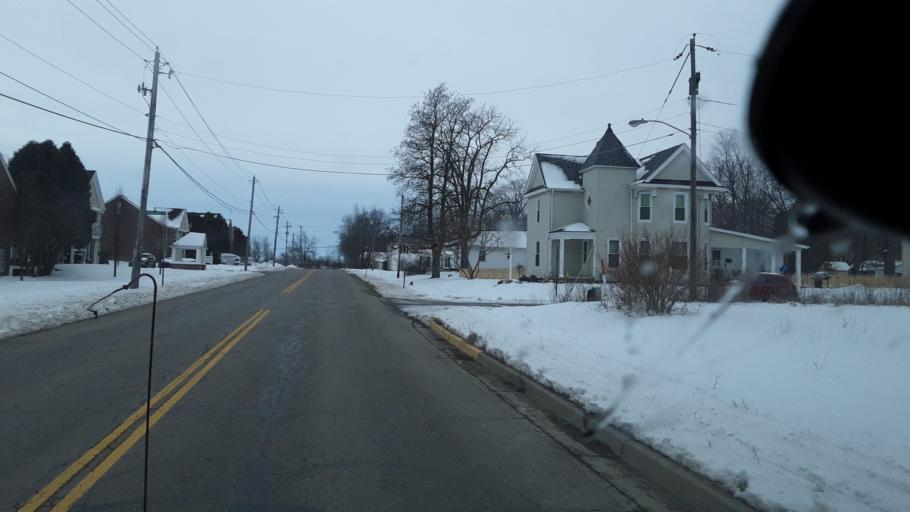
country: US
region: Ohio
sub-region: Madison County
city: London
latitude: 39.8780
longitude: -83.4539
